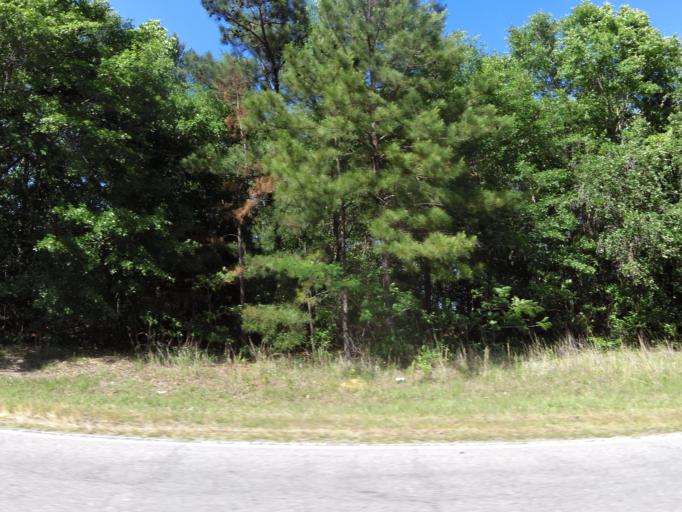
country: US
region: South Carolina
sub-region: Barnwell County
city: Williston
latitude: 33.3845
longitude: -81.3878
